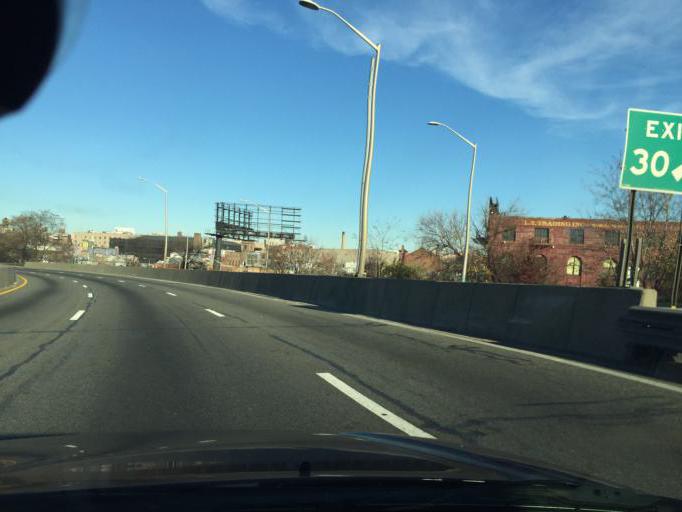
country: US
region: New York
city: New York City
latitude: 40.6963
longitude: -73.9635
